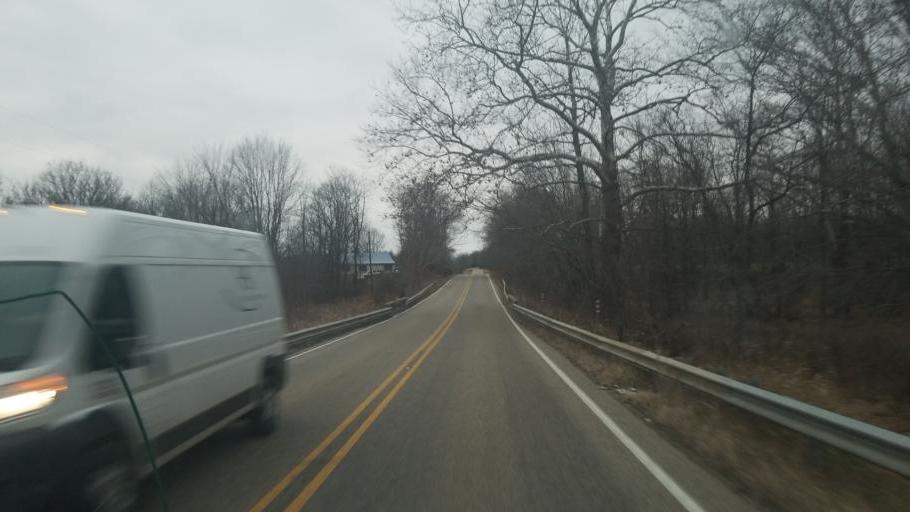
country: US
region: Indiana
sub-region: Owen County
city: Spencer
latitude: 39.3527
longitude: -86.9306
